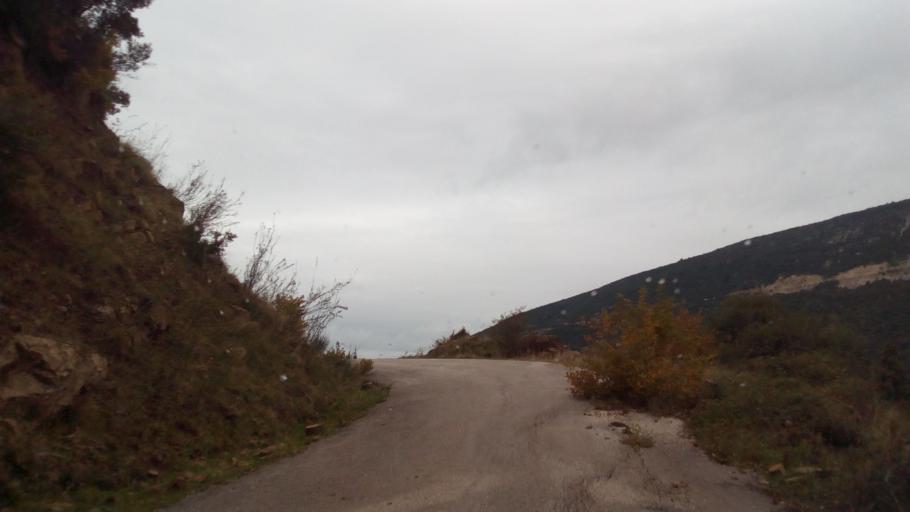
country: GR
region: West Greece
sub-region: Nomos Aitolias kai Akarnanias
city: Thermo
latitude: 38.6093
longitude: 21.8423
